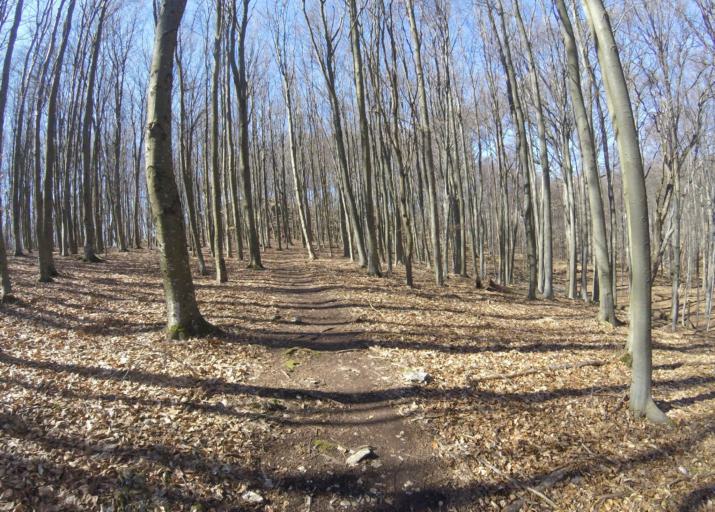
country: HU
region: Heves
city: Szilvasvarad
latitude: 48.0582
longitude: 20.4477
